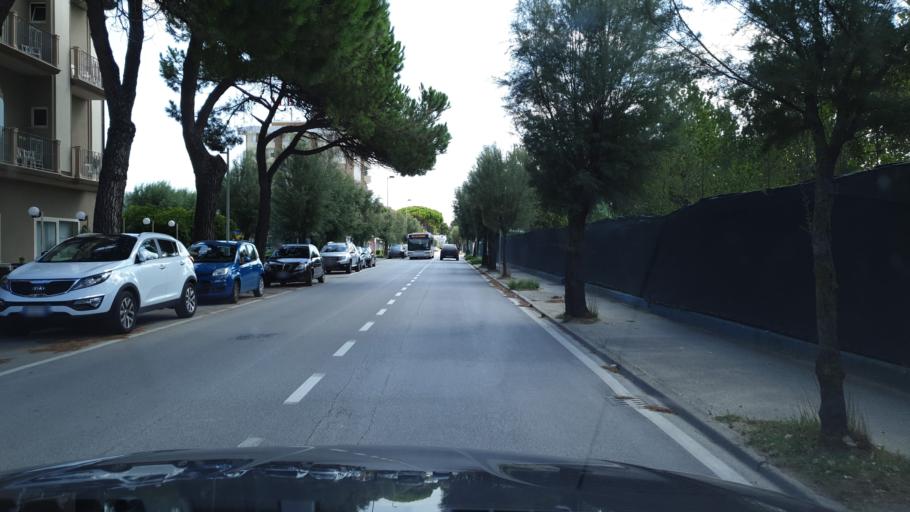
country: IT
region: Emilia-Romagna
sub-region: Provincia di Rimini
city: Misano Adriatico
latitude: 43.9901
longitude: 12.6807
